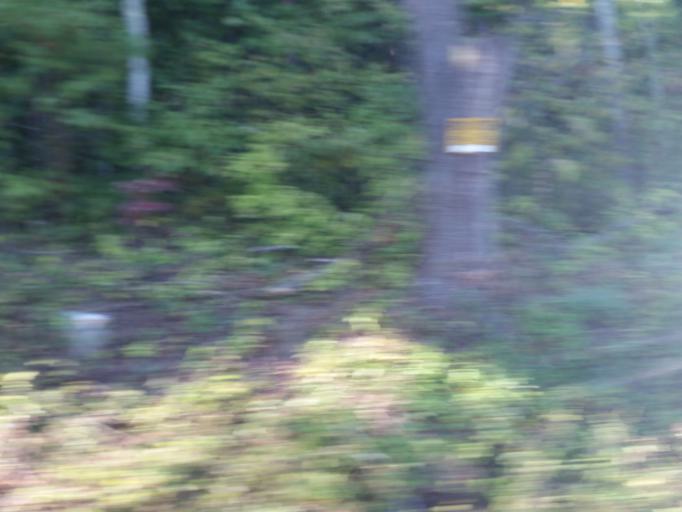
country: US
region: Tennessee
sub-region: Grainger County
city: Blaine
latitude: 36.2392
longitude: -83.6427
